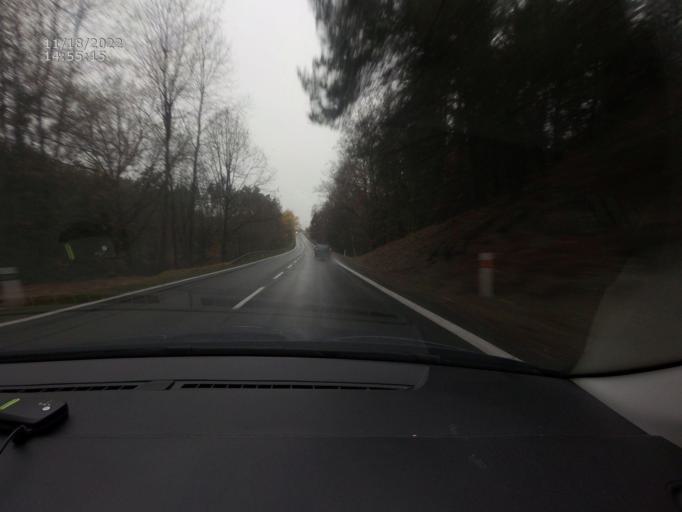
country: CZ
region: Jihocesky
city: Milevsko
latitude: 49.4654
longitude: 14.3142
